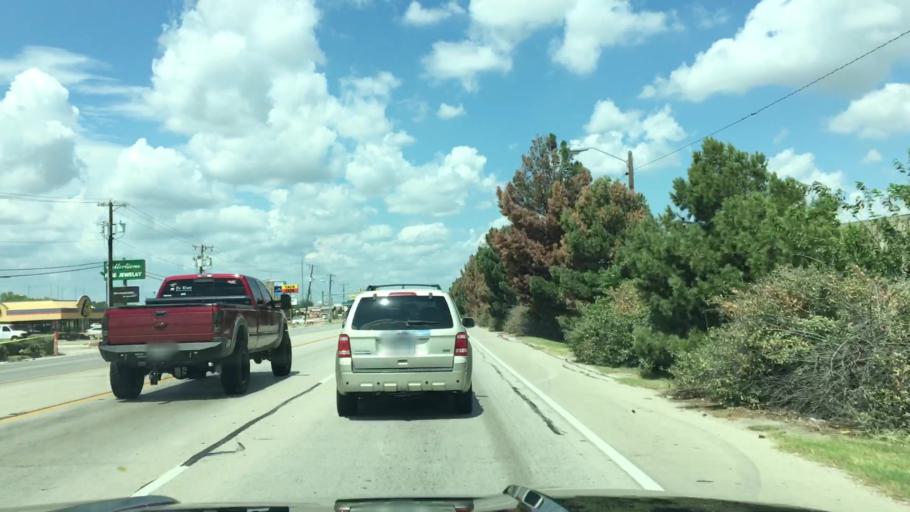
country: US
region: Texas
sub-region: Tarrant County
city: Saginaw
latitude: 32.8519
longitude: -97.3605
